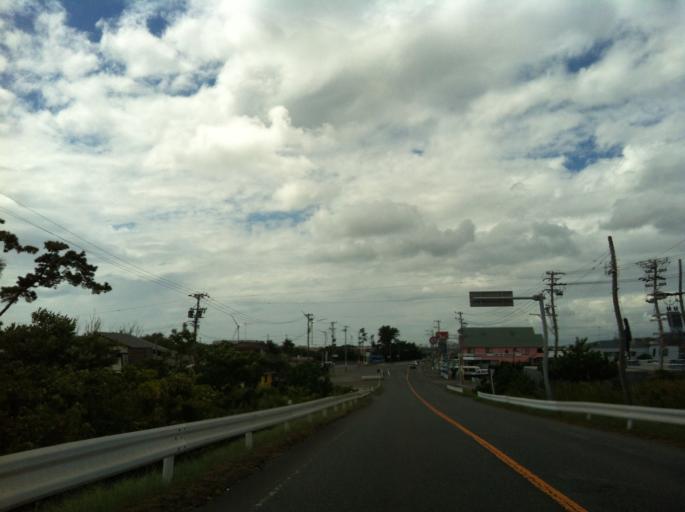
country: JP
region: Shizuoka
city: Kakegawa
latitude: 34.6541
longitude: 138.0651
